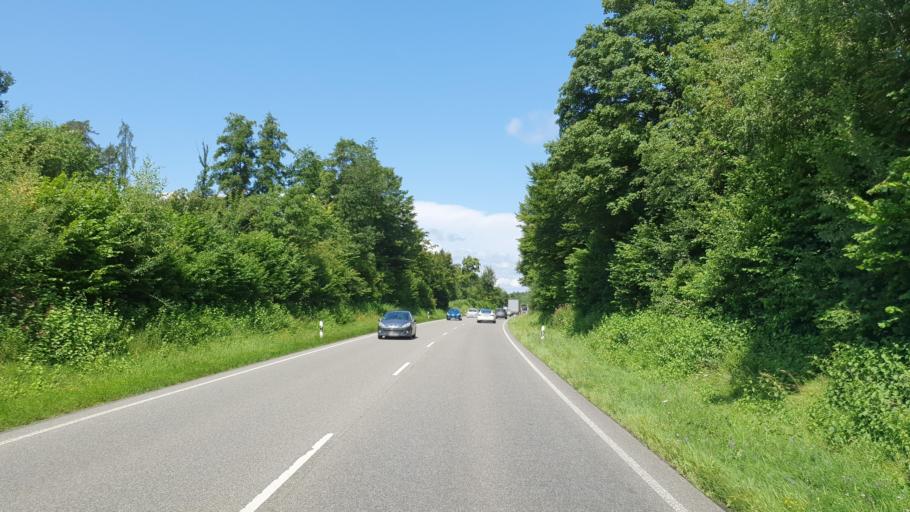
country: DE
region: Baden-Wuerttemberg
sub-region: Tuebingen Region
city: Daisendorf
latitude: 47.7076
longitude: 9.2613
